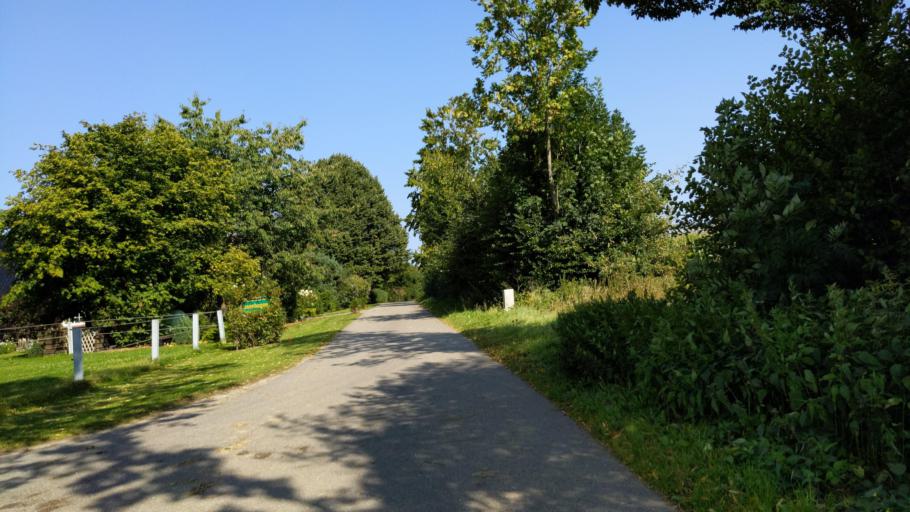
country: DE
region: Schleswig-Holstein
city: Wesenberg
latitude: 53.8308
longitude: 10.5485
